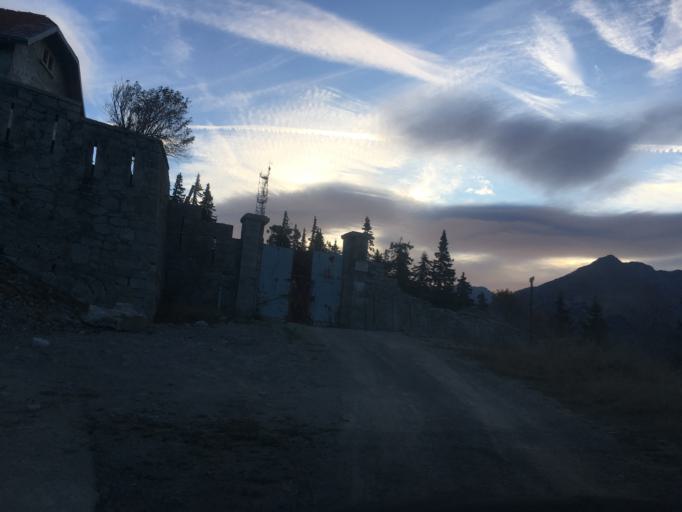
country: FR
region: Rhone-Alpes
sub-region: Departement de la Savoie
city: Modane
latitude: 45.2019
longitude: 6.6471
